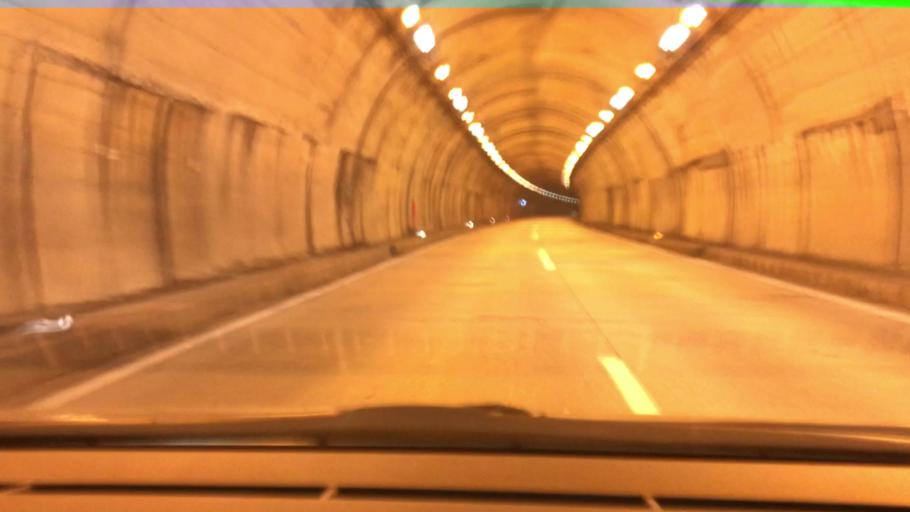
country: JP
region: Hyogo
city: Sasayama
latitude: 35.0594
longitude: 135.1842
